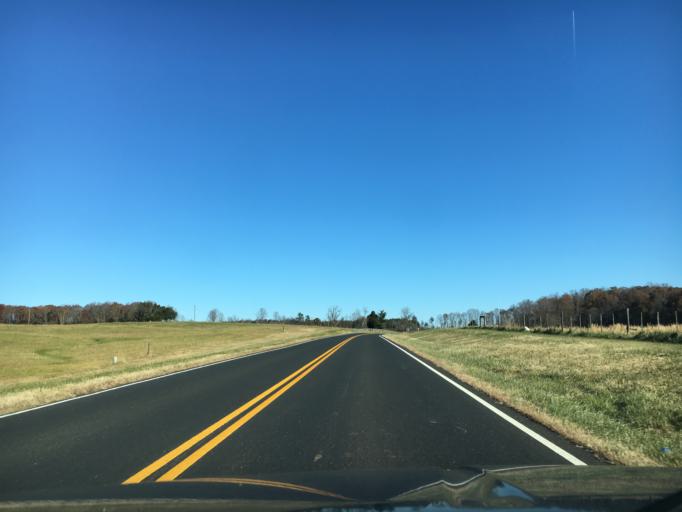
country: US
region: Virginia
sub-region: Appomattox County
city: Appomattox
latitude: 37.3883
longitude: -78.7869
